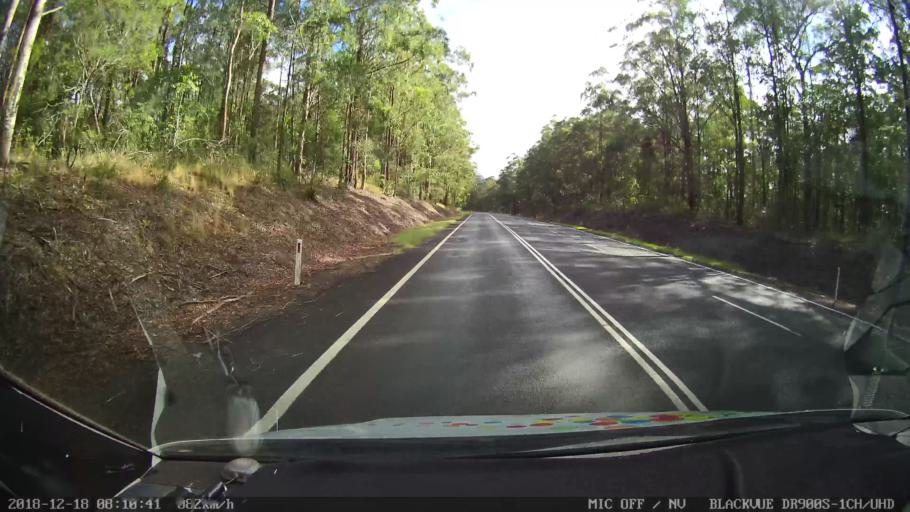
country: AU
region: New South Wales
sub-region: Kyogle
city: Kyogle
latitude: -28.3590
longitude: 152.6637
